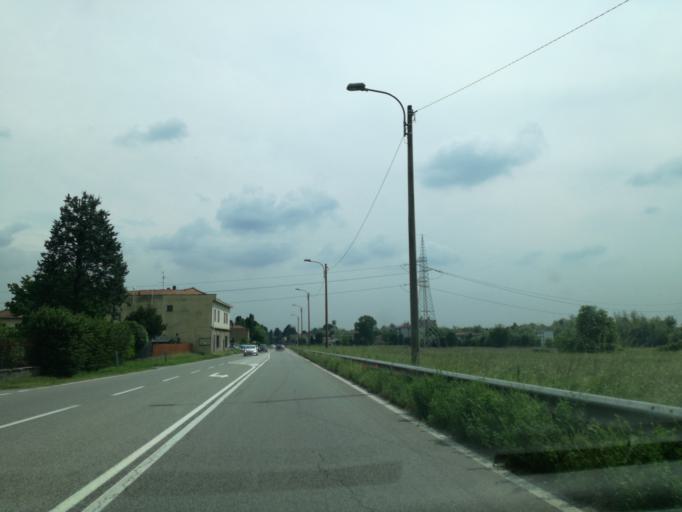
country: IT
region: Lombardy
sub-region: Provincia di Monza e Brianza
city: Carate Brianza
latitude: 45.6666
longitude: 9.2460
